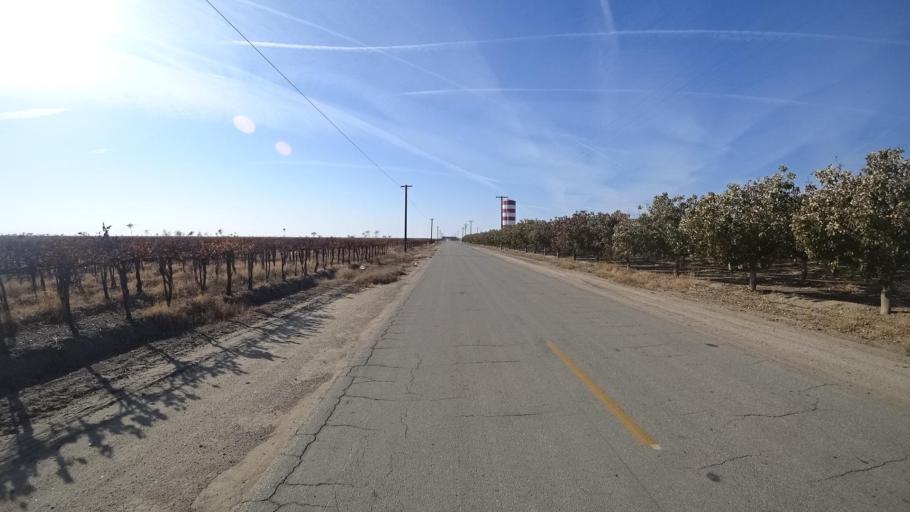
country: US
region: California
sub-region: Kern County
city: Wasco
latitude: 35.7032
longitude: -119.3366
